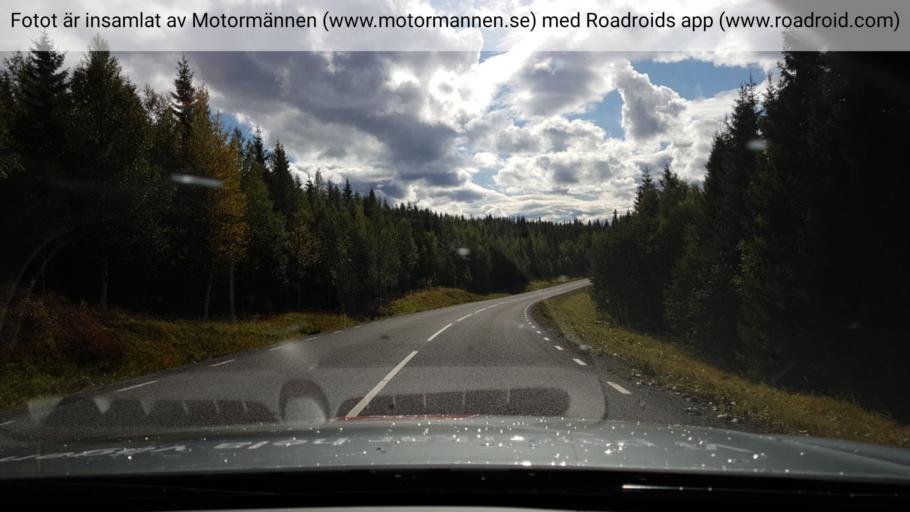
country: SE
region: Jaemtland
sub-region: Are Kommun
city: Are
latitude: 63.5999
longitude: 13.1078
